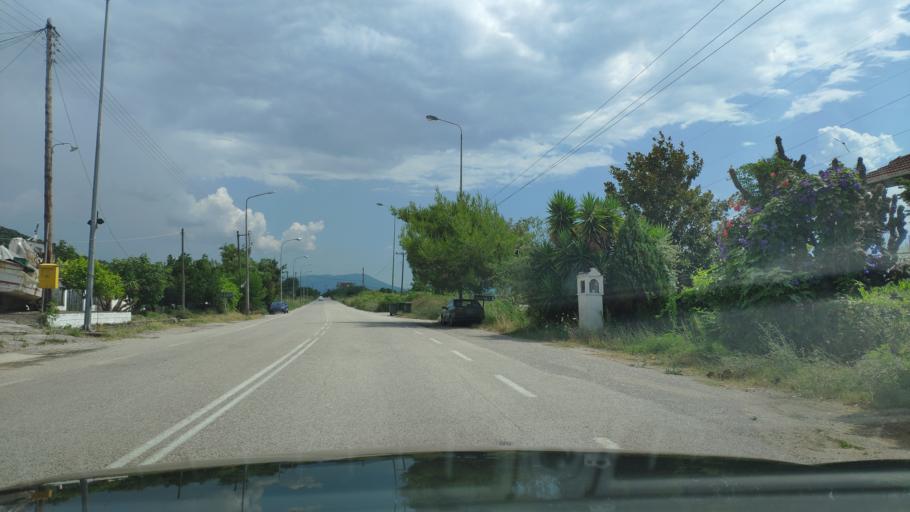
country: GR
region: West Greece
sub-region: Nomos Aitolias kai Akarnanias
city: Krikellos
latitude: 38.9710
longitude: 21.1676
